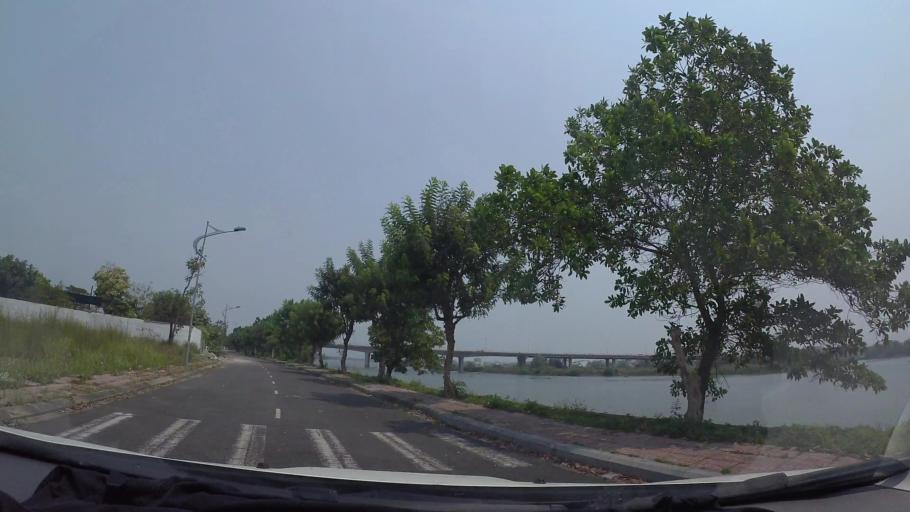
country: VN
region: Da Nang
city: Cam Le
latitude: 16.0139
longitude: 108.2113
